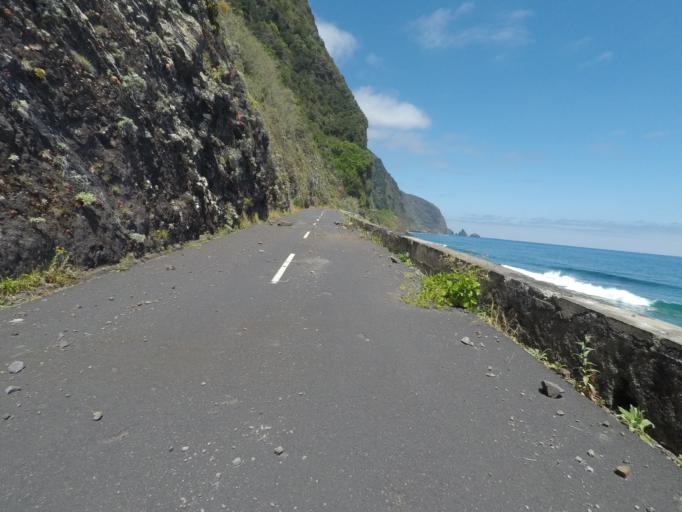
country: PT
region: Madeira
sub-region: Porto Moniz
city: Porto Moniz
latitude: 32.8282
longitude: -17.1263
